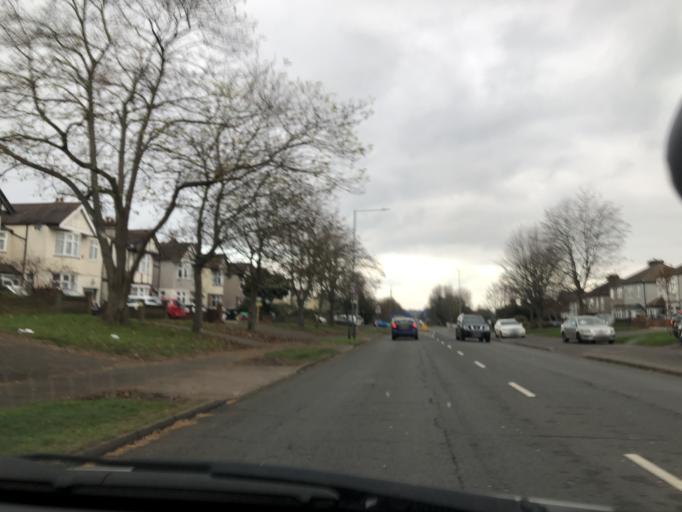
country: GB
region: England
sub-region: Kent
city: Dartford
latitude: 51.4434
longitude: 0.1943
